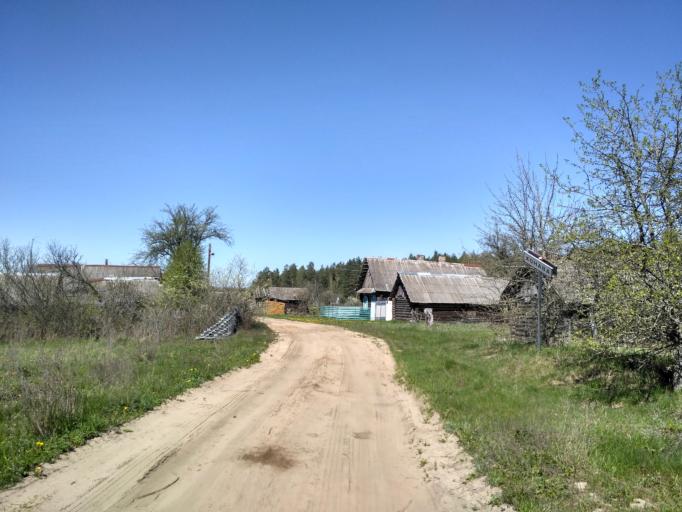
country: BY
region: Minsk
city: Horad Barysaw
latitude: 54.5023
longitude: 28.4997
